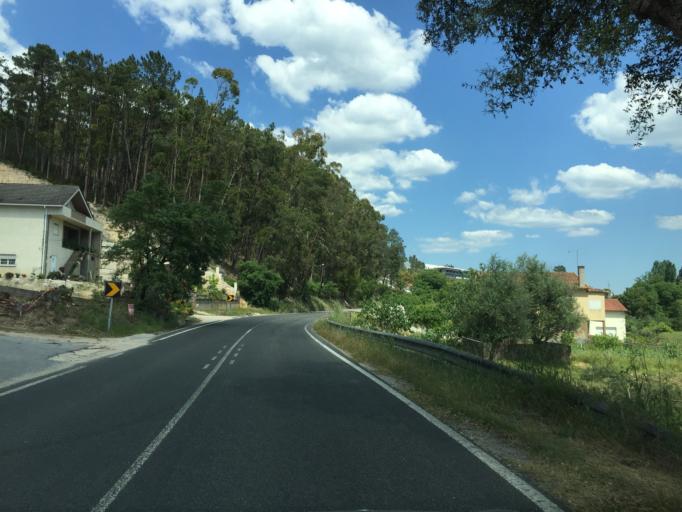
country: PT
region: Santarem
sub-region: Ourem
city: Ourem
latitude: 39.6536
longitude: -8.6007
